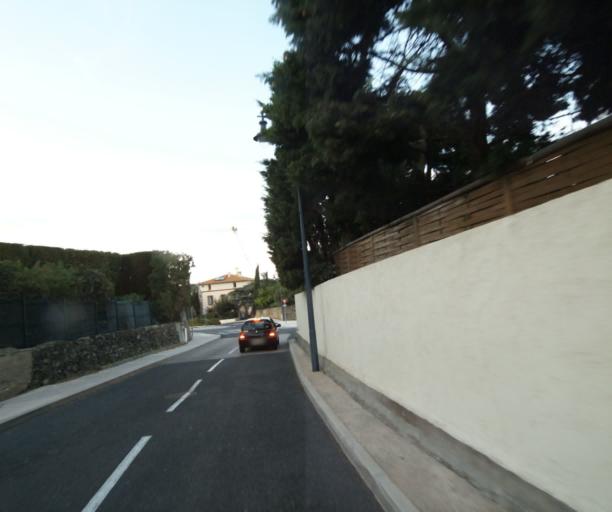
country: FR
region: Languedoc-Roussillon
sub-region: Departement des Pyrenees-Orientales
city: Portvendres
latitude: 42.5149
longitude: 3.1089
